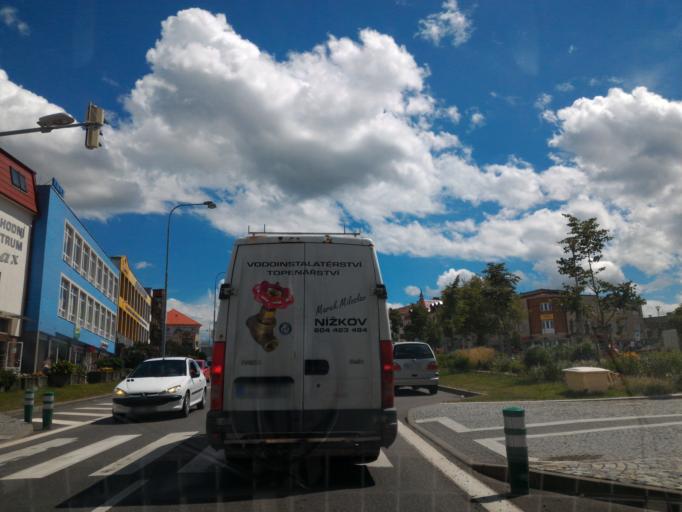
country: CZ
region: Vysocina
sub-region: Okres Zd'ar nad Sazavou
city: Zd'ar nad Sazavou
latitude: 49.5630
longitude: 15.9400
